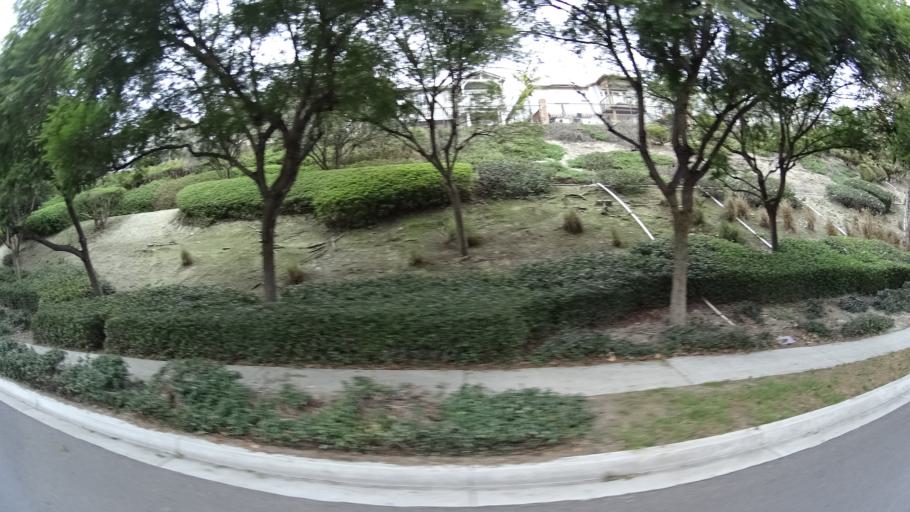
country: US
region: California
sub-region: Orange County
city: Aliso Viejo
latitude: 33.5692
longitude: -117.7374
